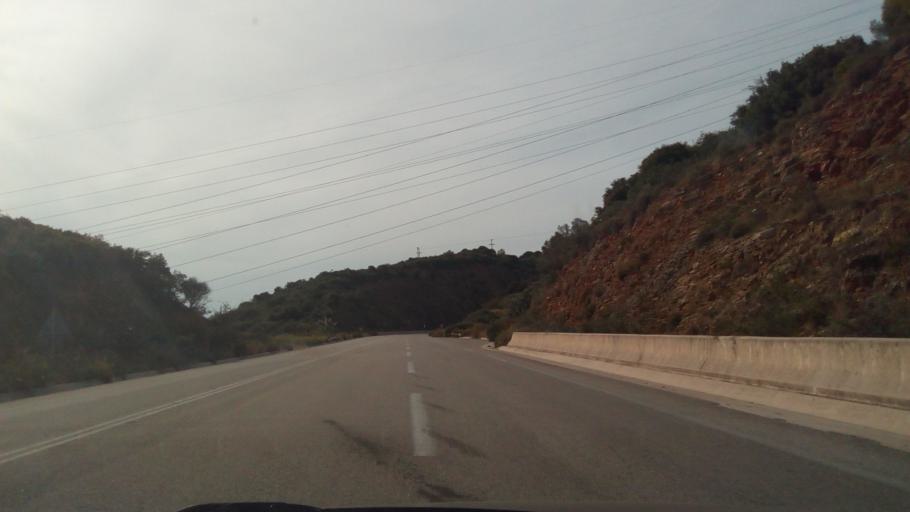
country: GR
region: West Greece
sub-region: Nomos Aitolias kai Akarnanias
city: Nafpaktos
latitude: 38.4040
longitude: 21.8363
